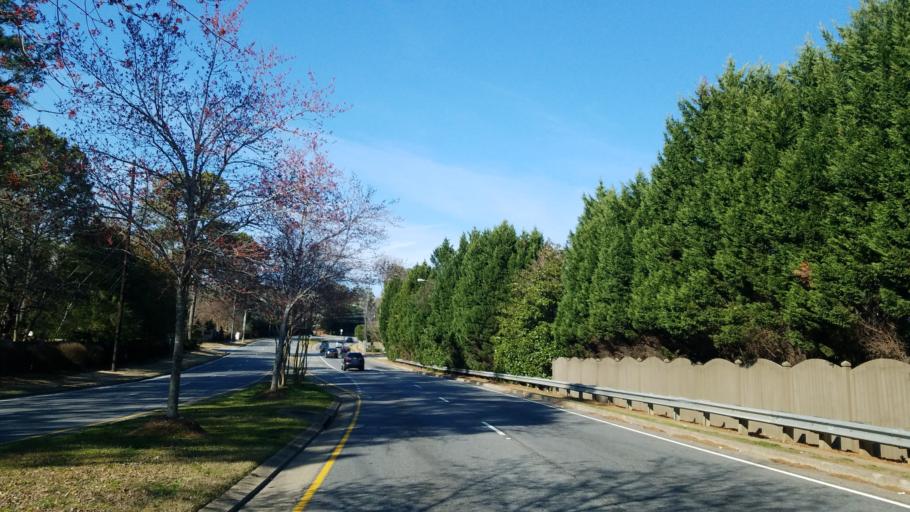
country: US
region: Georgia
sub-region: Fulton County
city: Roswell
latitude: 34.0095
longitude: -84.4329
